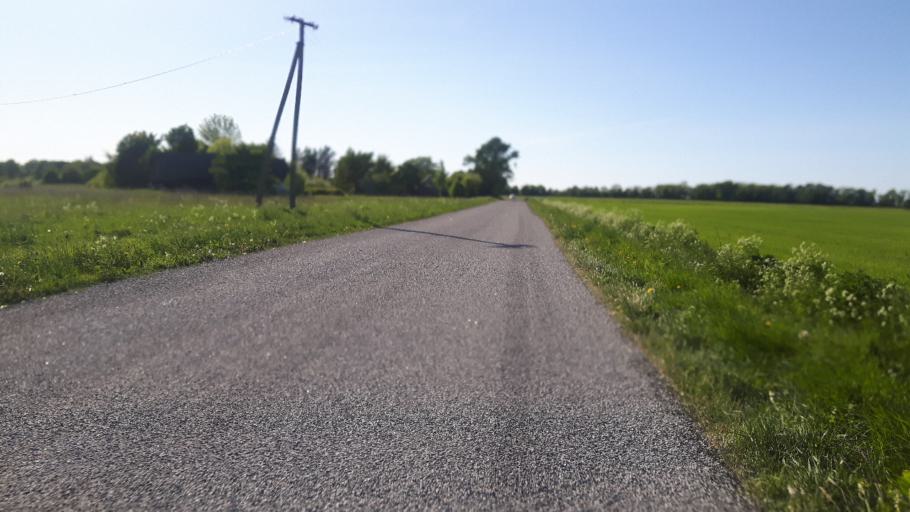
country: EE
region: Ida-Virumaa
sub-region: Kohtla-Jaerve linn
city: Kohtla-Jarve
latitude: 59.4363
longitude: 27.2001
